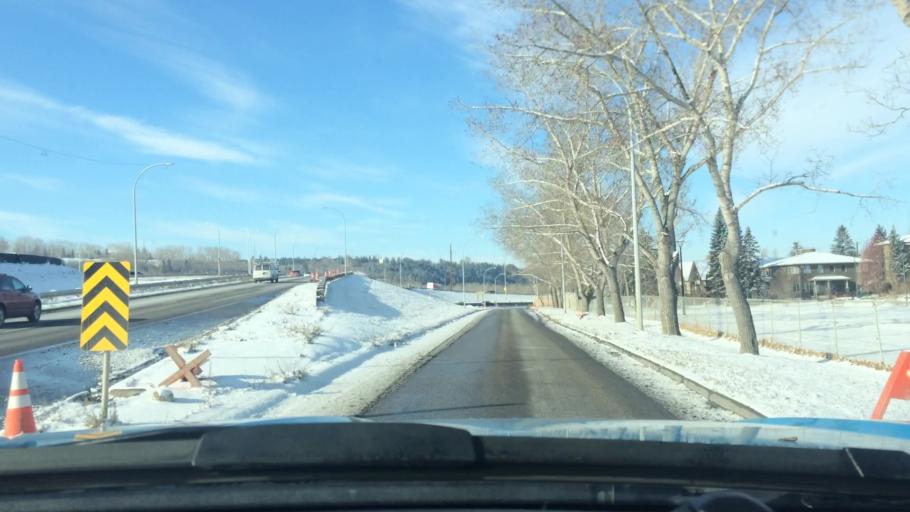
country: CA
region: Alberta
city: Calgary
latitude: 51.0497
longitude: -114.1135
